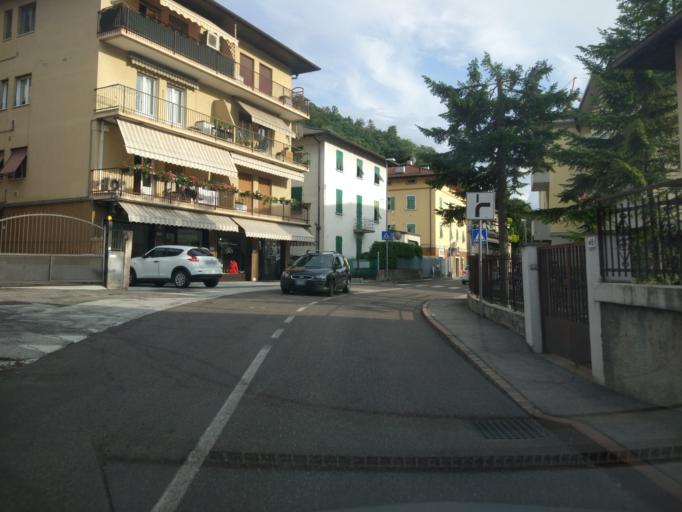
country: IT
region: Trentino-Alto Adige
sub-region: Provincia di Trento
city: Trento
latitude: 46.0852
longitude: 11.1228
